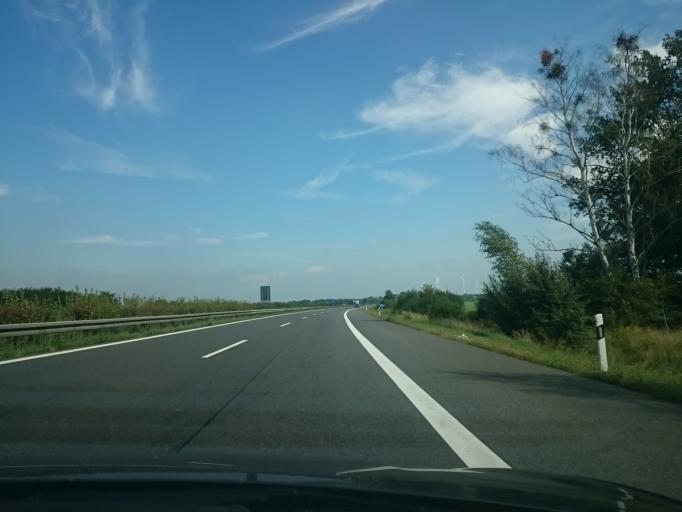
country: DE
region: Brandenburg
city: Grossraschen
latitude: 51.5807
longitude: 13.9334
